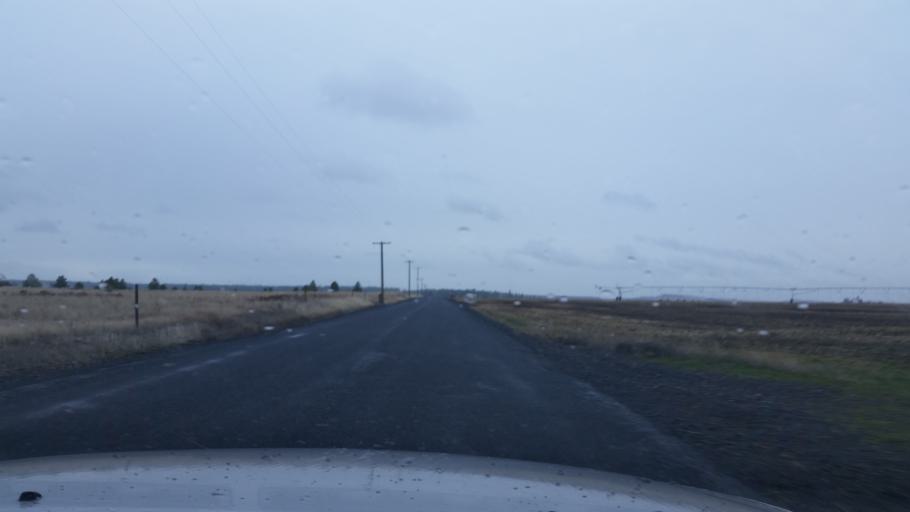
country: US
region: Washington
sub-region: Spokane County
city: Medical Lake
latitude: 47.6145
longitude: -117.7700
